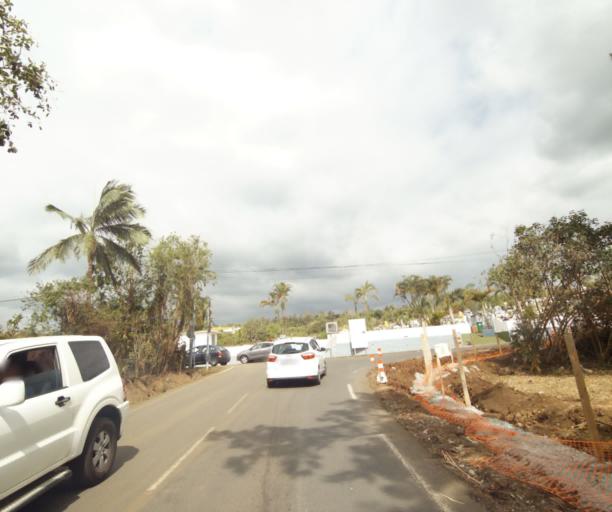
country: RE
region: Reunion
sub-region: Reunion
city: Saint-Paul
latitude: -21.0370
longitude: 55.2886
